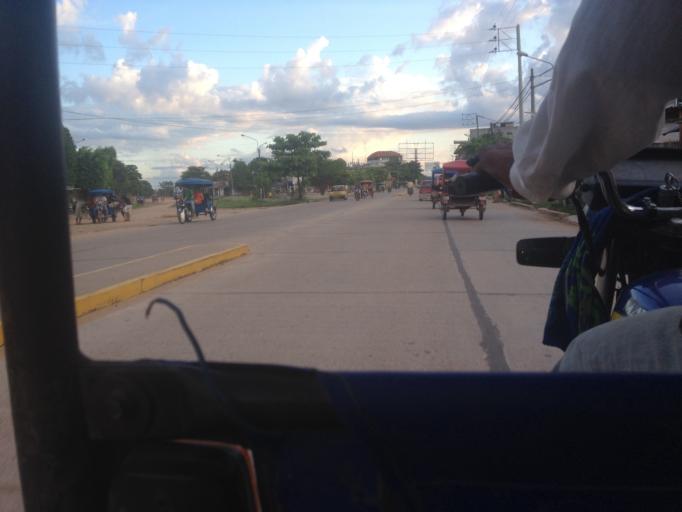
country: PE
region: Ucayali
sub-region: Provincia de Coronel Portillo
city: Pucallpa
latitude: -8.3772
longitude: -74.5687
